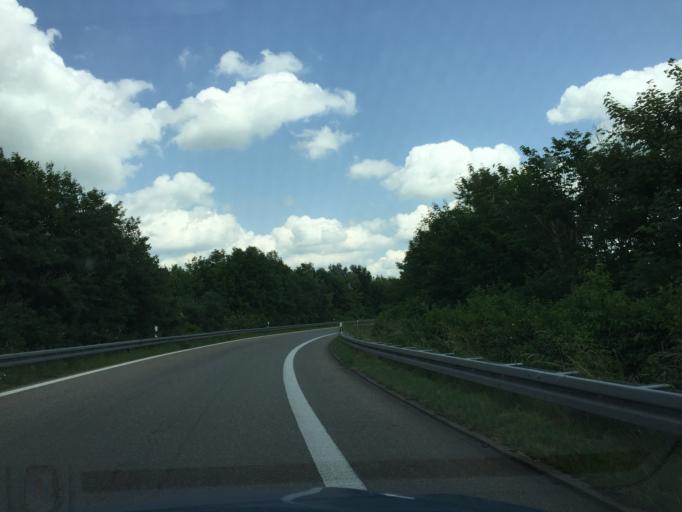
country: DE
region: Baden-Wuerttemberg
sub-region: Tuebingen Region
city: Langenau
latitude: 48.4635
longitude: 10.1185
